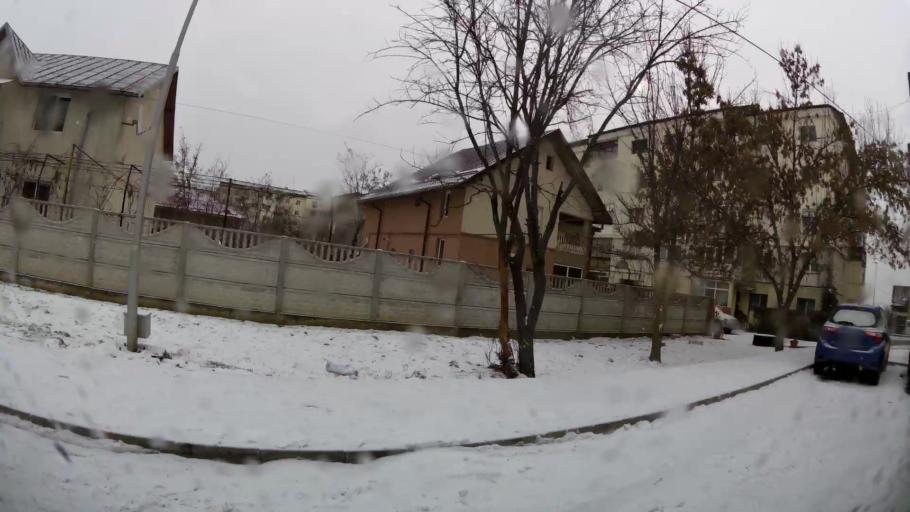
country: RO
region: Dambovita
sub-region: Municipiul Targoviste
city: Targoviste
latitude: 44.9138
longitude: 25.4734
